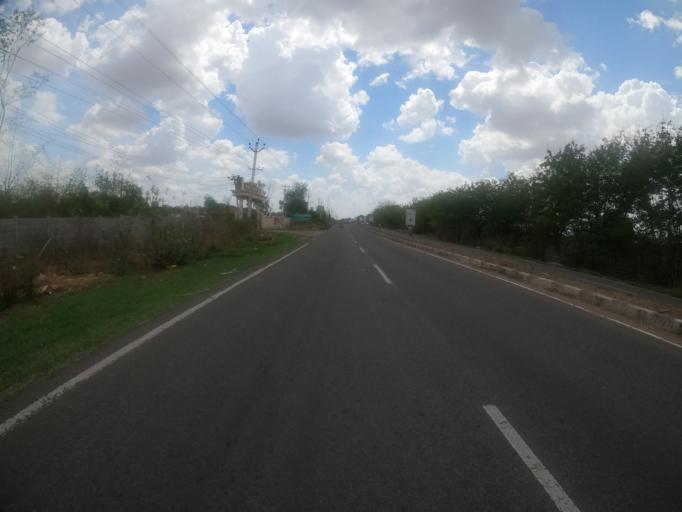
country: IN
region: Telangana
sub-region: Rangareddi
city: Sriramnagar
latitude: 17.3311
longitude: 78.2935
